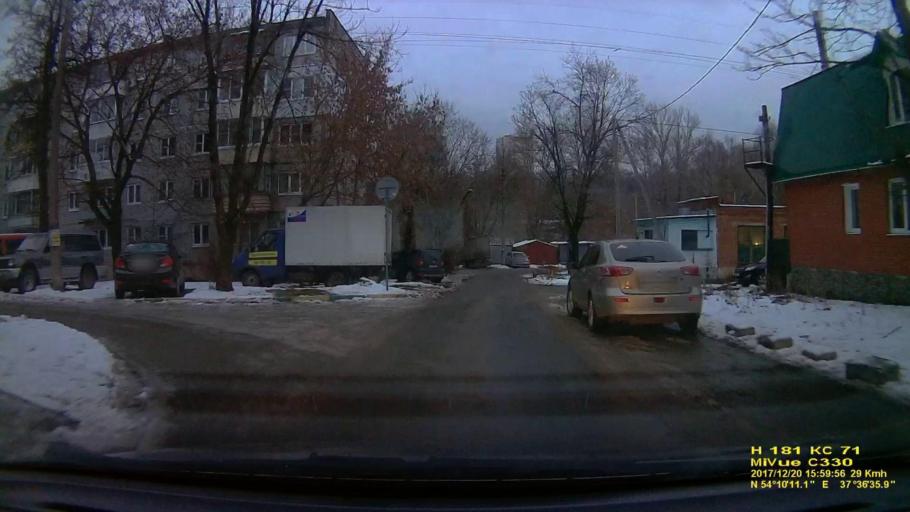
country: RU
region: Tula
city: Tula
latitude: 54.1699
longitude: 37.6100
